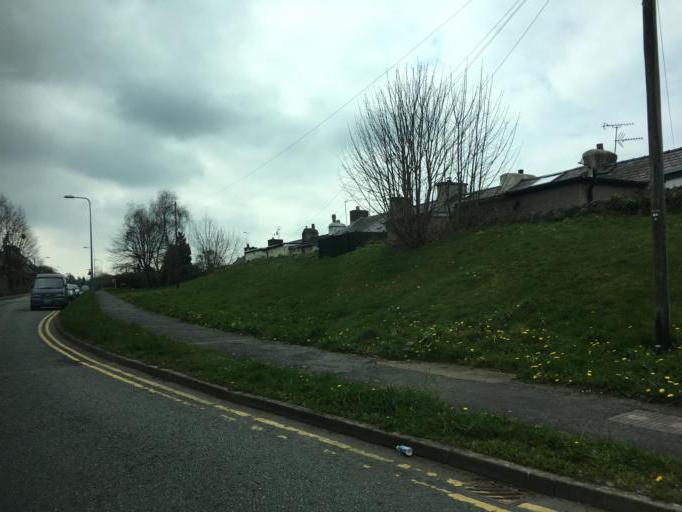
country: GB
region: Wales
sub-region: Gwynedd
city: Y Felinheli
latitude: 53.1834
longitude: -4.2097
